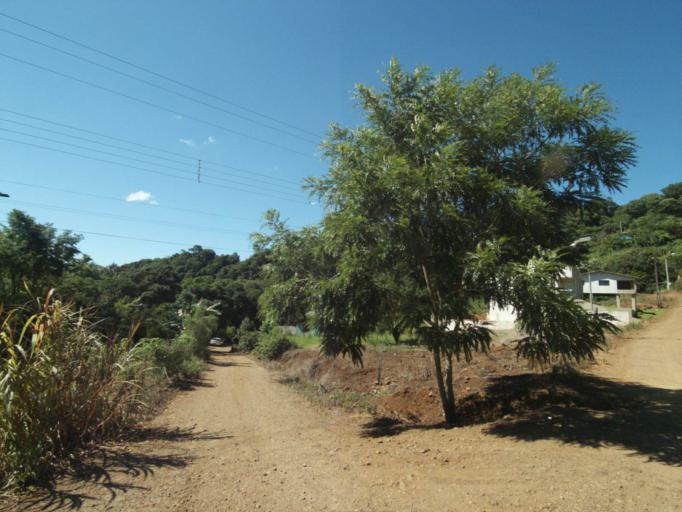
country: BR
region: Parana
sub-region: Ampere
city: Ampere
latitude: -26.1691
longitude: -53.3615
